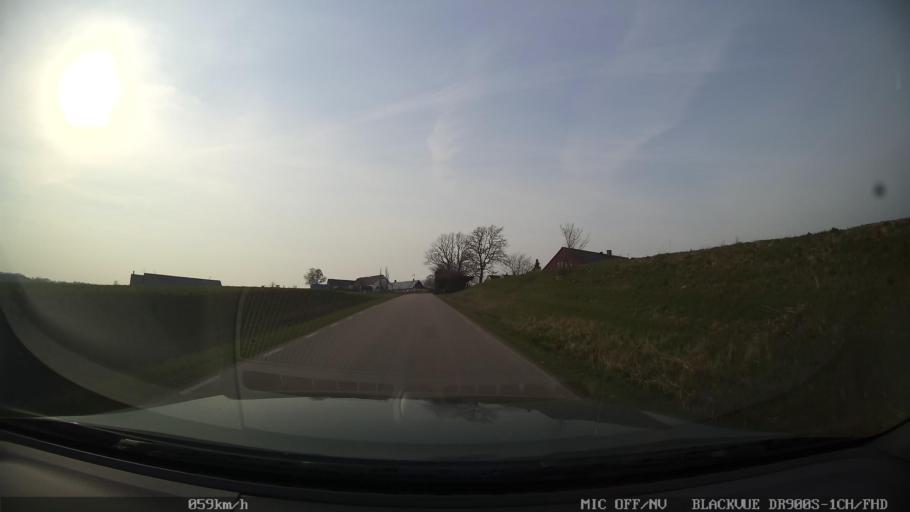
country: SE
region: Skane
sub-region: Ystads Kommun
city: Ystad
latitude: 55.4659
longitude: 13.8155
